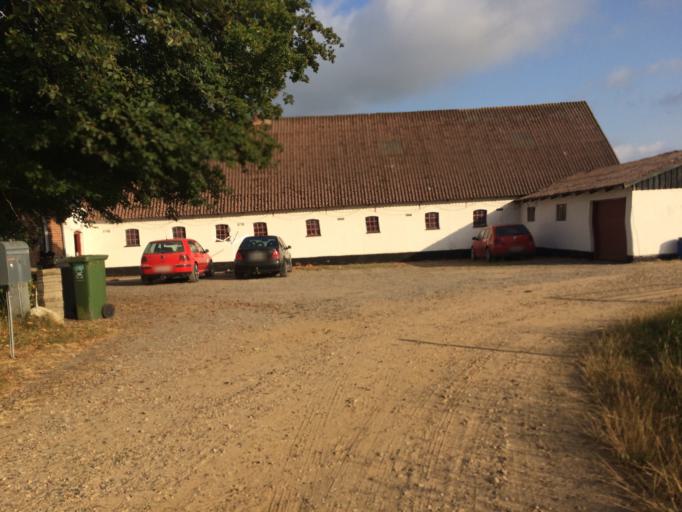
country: DK
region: Central Jutland
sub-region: Holstebro Kommune
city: Vinderup
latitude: 56.6168
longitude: 8.7136
